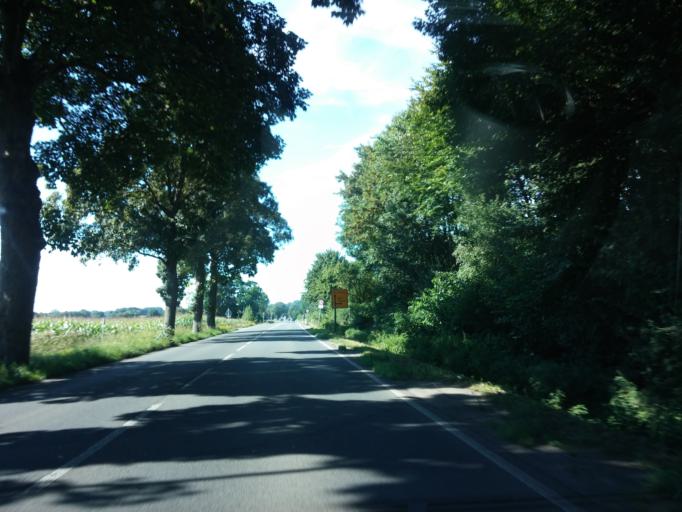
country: DE
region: North Rhine-Westphalia
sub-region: Regierungsbezirk Munster
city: Gladbeck
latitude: 51.6185
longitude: 7.0174
